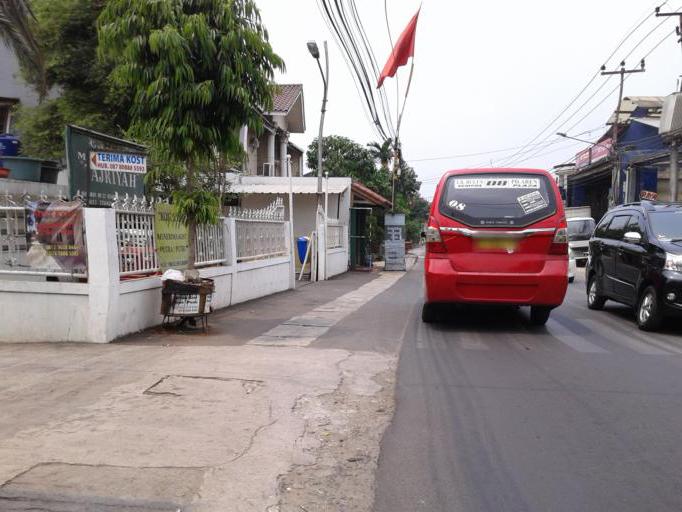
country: ID
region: Banten
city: South Tangerang
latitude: -6.2866
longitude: 106.7601
